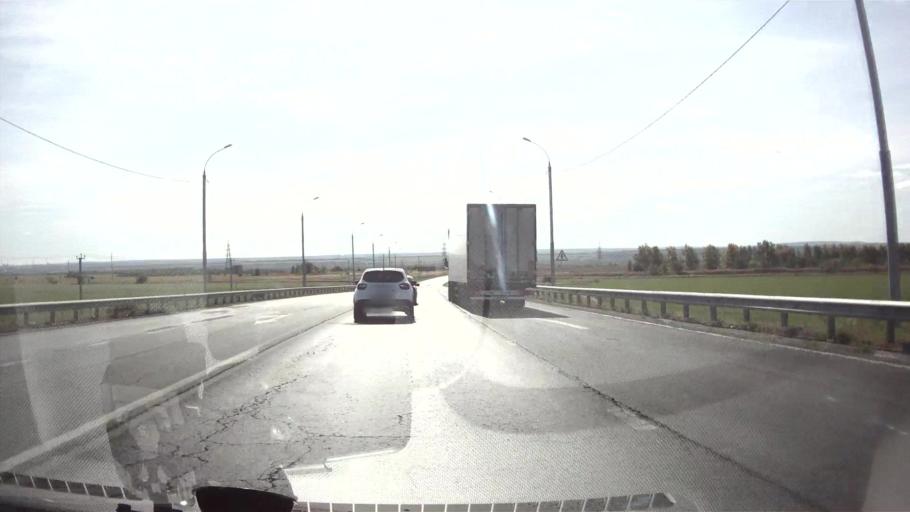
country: RU
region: Samara
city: Varlamovo
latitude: 53.1910
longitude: 48.2922
